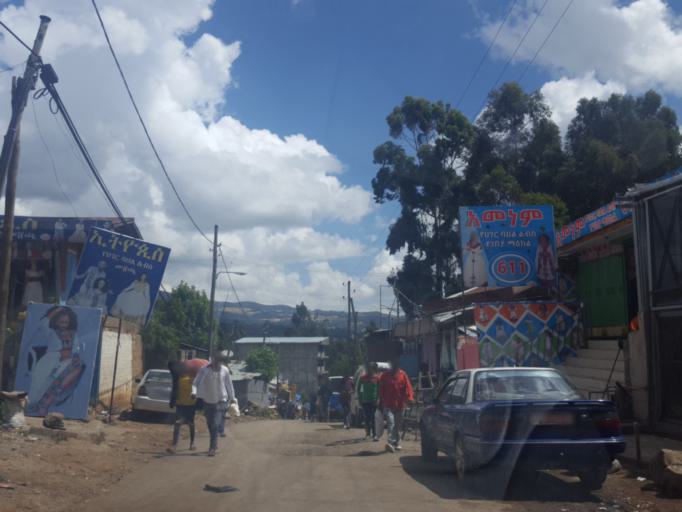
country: ET
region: Adis Abeba
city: Addis Ababa
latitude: 9.0614
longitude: 38.7618
